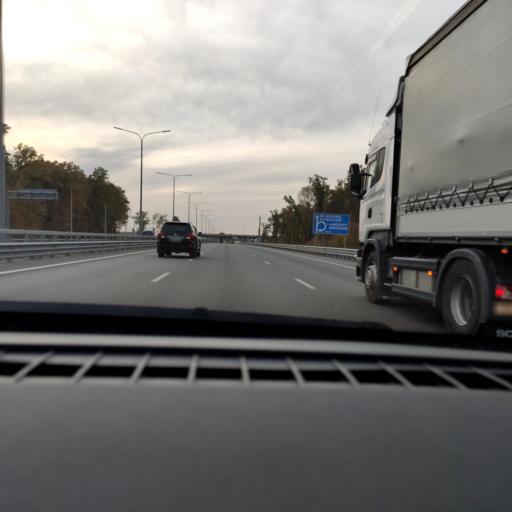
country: RU
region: Voronezj
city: Podgornoye
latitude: 51.8367
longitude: 39.2248
